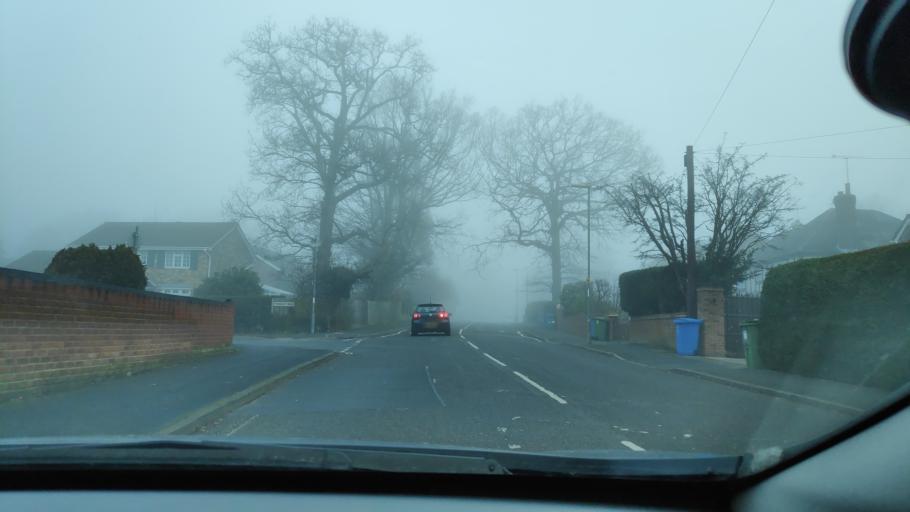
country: GB
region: England
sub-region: Hampshire
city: Farnborough
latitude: 51.2877
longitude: -0.7450
